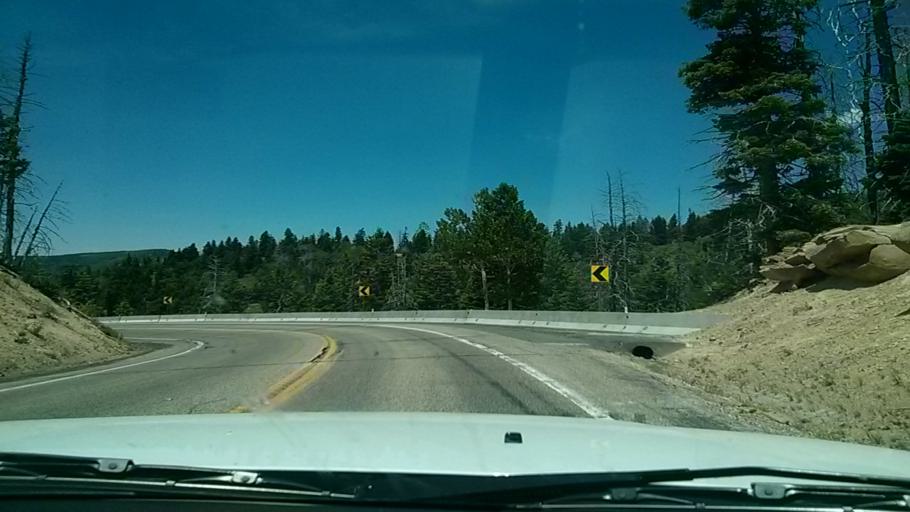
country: US
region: Utah
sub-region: Iron County
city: Cedar City
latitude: 37.5925
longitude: -112.8982
